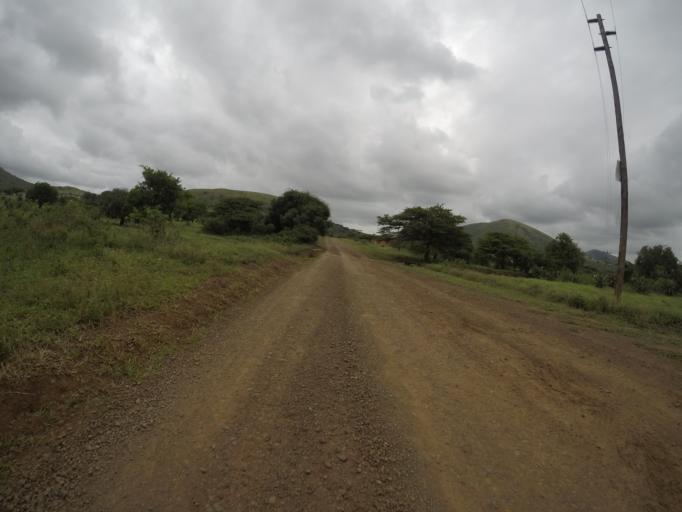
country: ZA
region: KwaZulu-Natal
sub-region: uThungulu District Municipality
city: Empangeni
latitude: -28.6044
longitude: 31.8702
